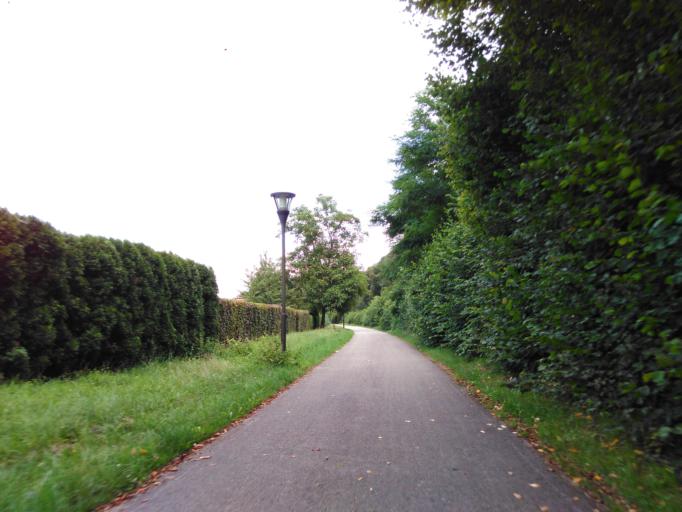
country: DE
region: Rheinland-Pfalz
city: Menningen
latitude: 49.8166
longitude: 6.4766
